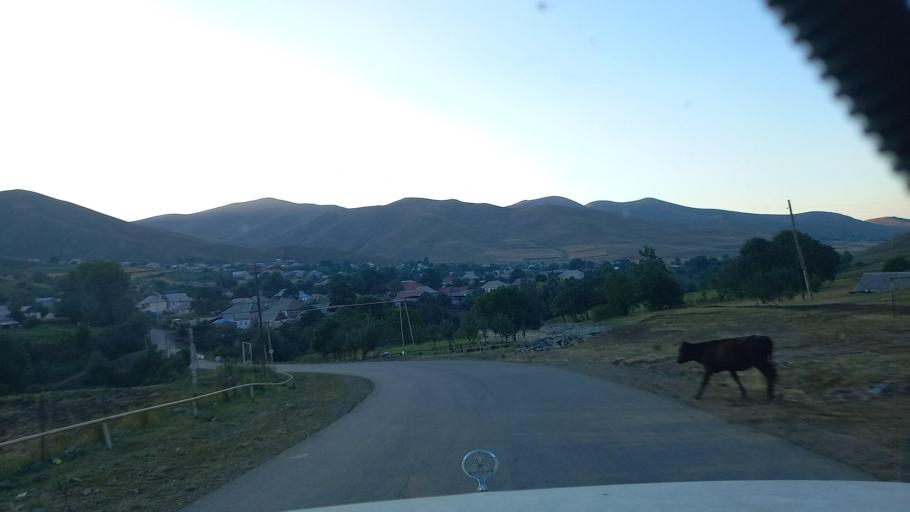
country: AZ
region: Tovuz
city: Cobansignaq
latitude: 40.6837
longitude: 45.7668
